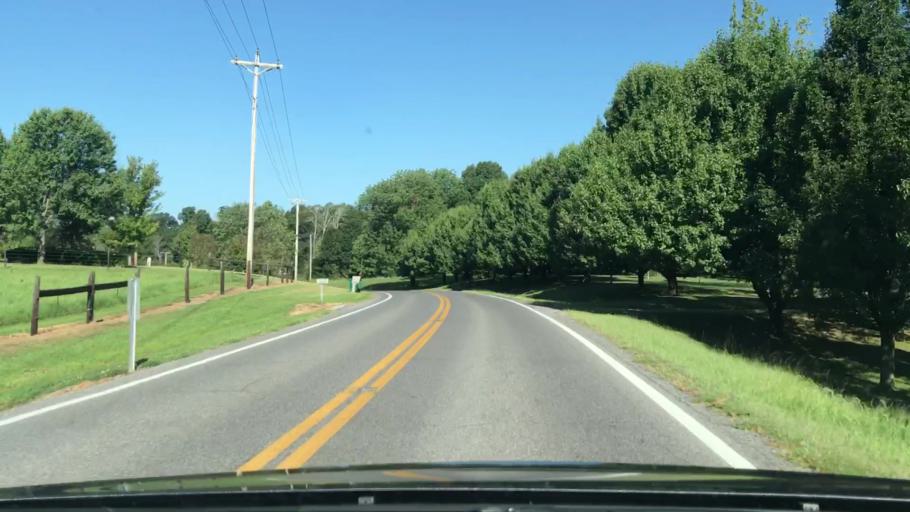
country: US
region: Kentucky
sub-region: Graves County
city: Mayfield
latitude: 36.7786
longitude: -88.5117
